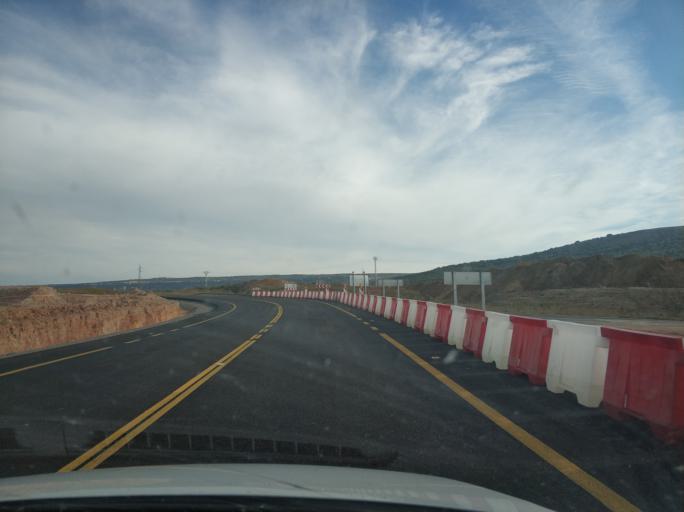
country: ES
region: Castille and Leon
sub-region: Provincia de Palencia
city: Pomar de Valdivia
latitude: 42.7573
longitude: -4.1798
